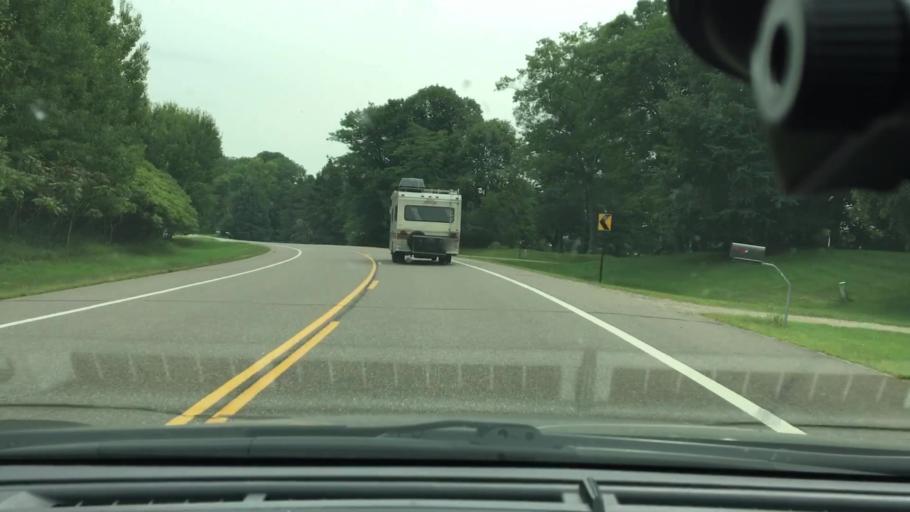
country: US
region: Minnesota
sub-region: Crow Wing County
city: Crosby
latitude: 46.4082
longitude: -93.8220
